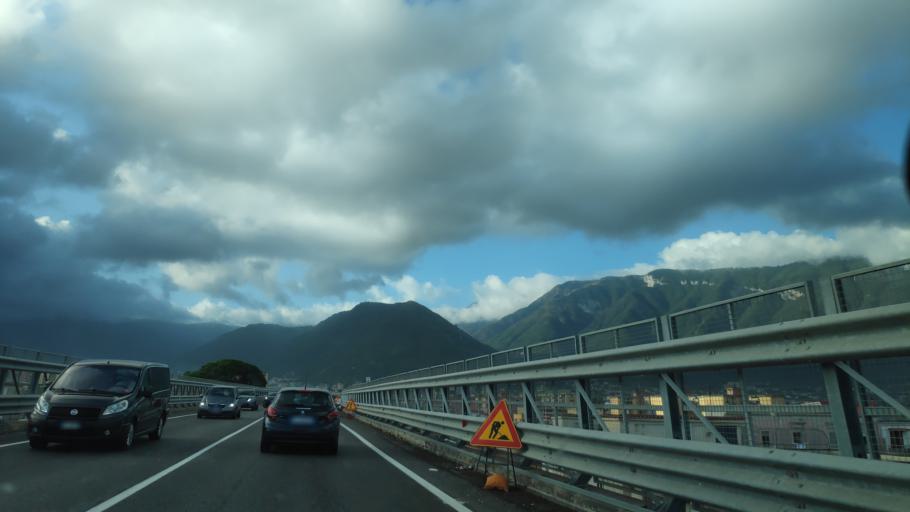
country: IT
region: Campania
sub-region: Provincia di Napoli
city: Castellammare di Stabia
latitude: 40.7140
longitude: 14.4962
